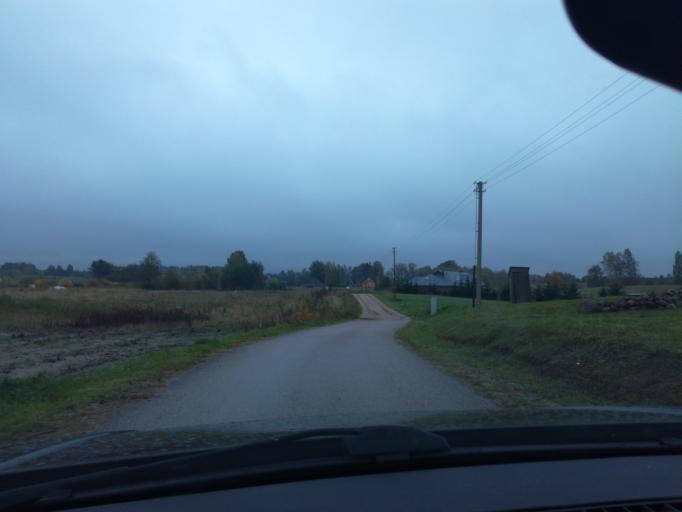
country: LT
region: Alytaus apskritis
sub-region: Alytus
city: Alytus
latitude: 54.4059
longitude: 24.0948
